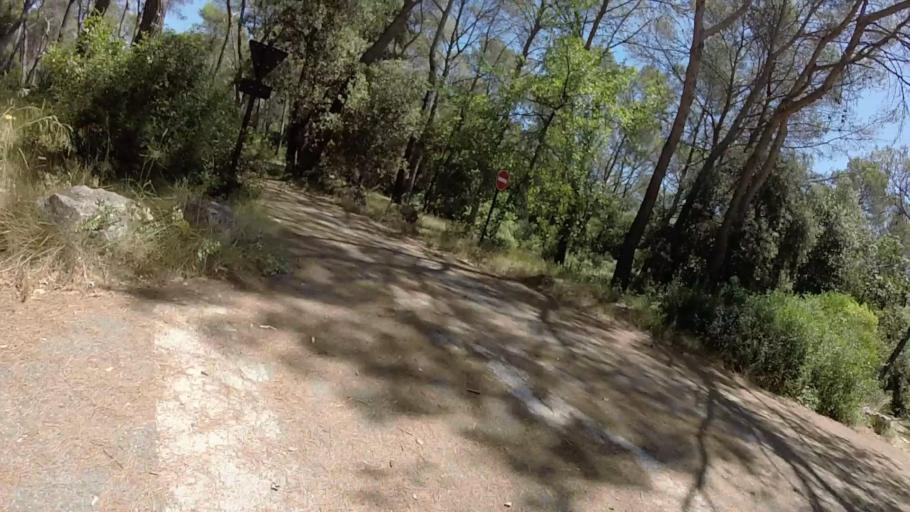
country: FR
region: Provence-Alpes-Cote d'Azur
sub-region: Departement des Alpes-Maritimes
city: Vallauris
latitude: 43.6115
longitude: 7.0438
